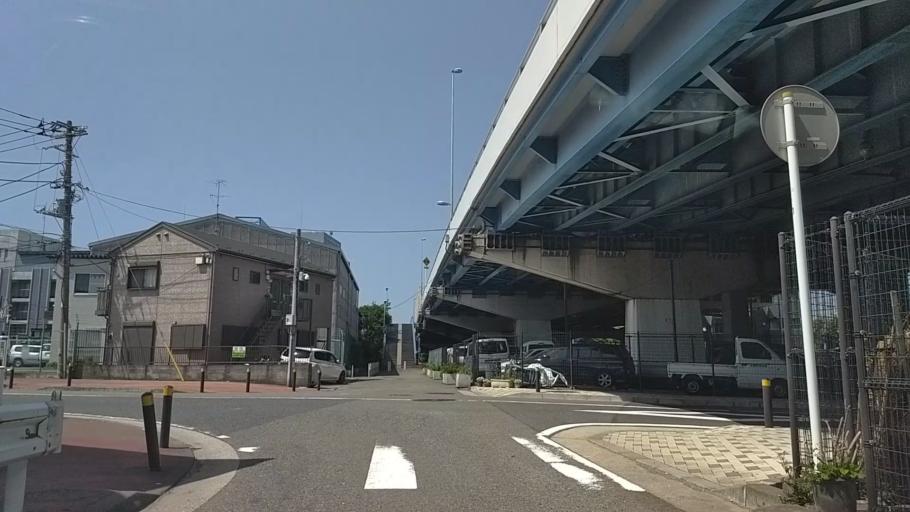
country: JP
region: Kanagawa
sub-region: Kawasaki-shi
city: Kawasaki
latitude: 35.4961
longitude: 139.6837
